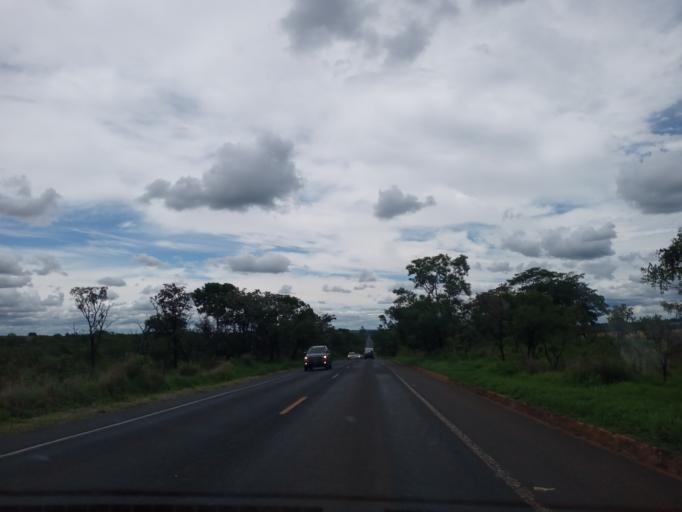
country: BR
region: Minas Gerais
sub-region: Uberlandia
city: Uberlandia
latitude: -19.1871
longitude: -47.8729
